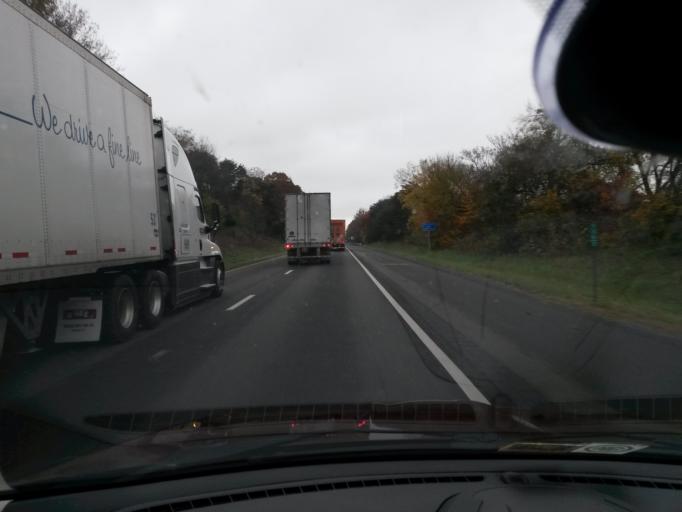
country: US
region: Virginia
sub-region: City of Salem
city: Salem
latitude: 37.2892
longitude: -80.1148
